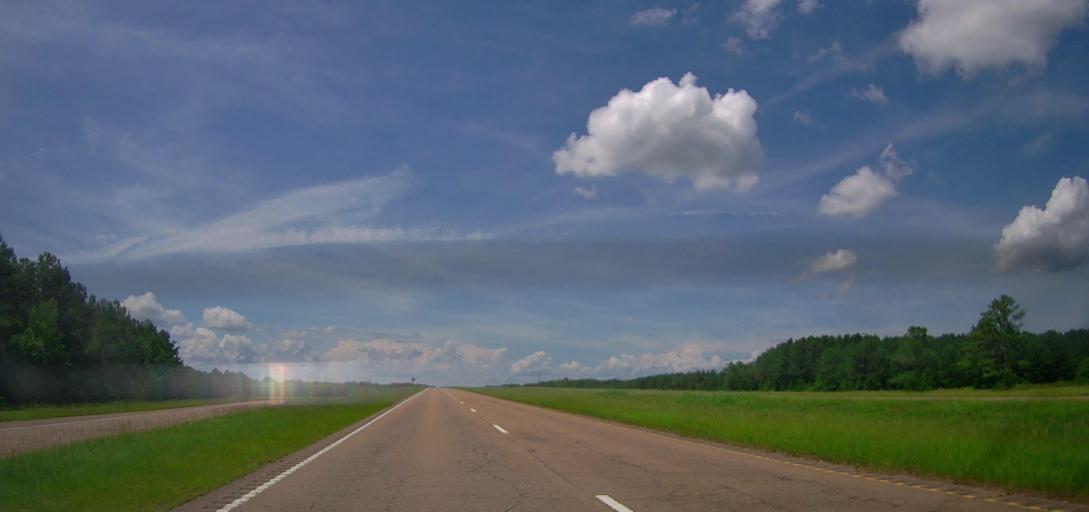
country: US
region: Mississippi
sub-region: Monroe County
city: Aberdeen
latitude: 33.8362
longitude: -88.5900
